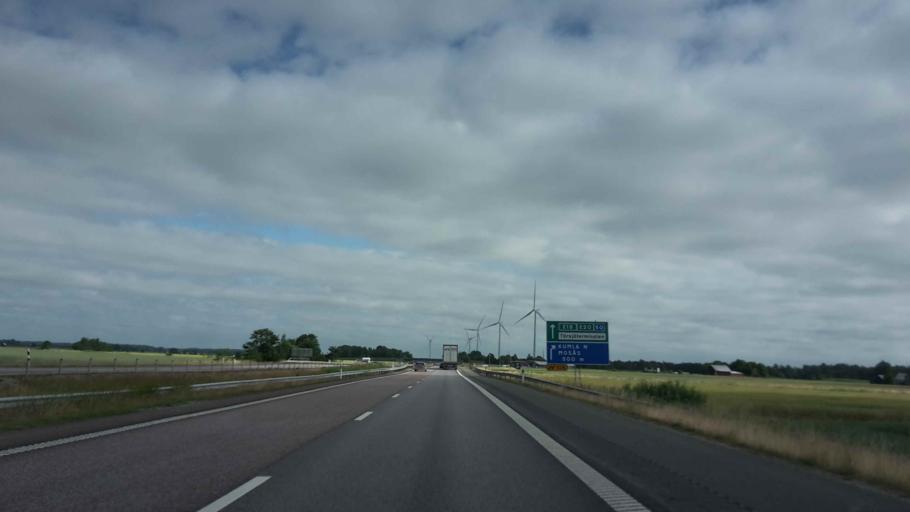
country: SE
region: OErebro
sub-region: Kumla Kommun
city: Kumla
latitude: 59.1578
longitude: 15.1043
